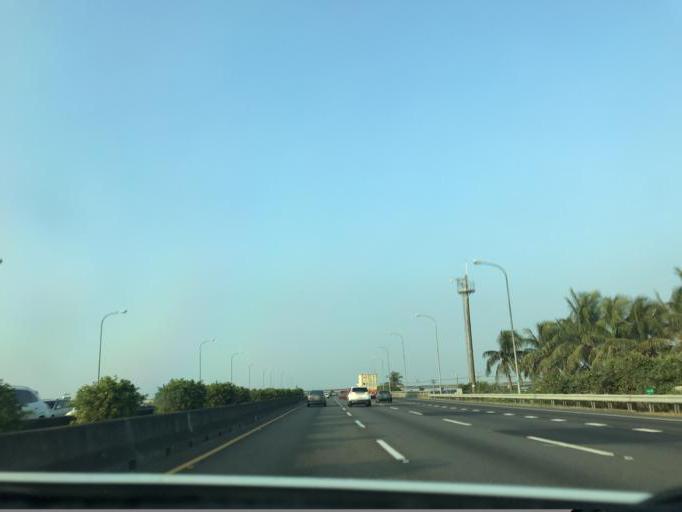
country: TW
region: Taiwan
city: Xinying
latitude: 23.2111
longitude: 120.2374
